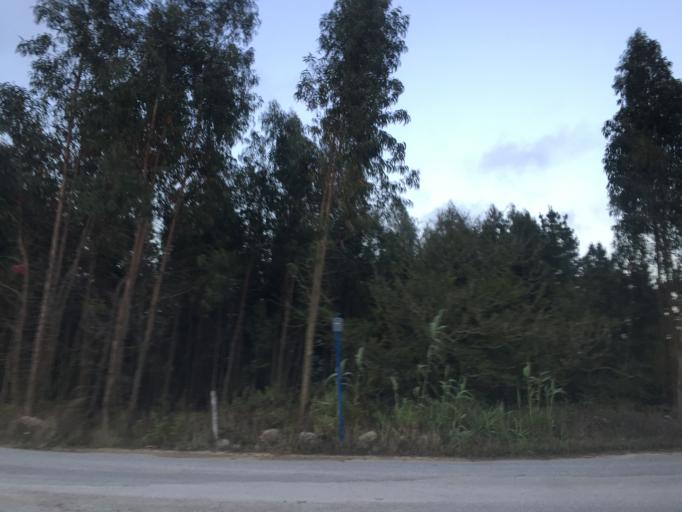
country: PT
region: Leiria
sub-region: Bombarral
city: Bombarral
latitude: 39.2936
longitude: -9.2240
